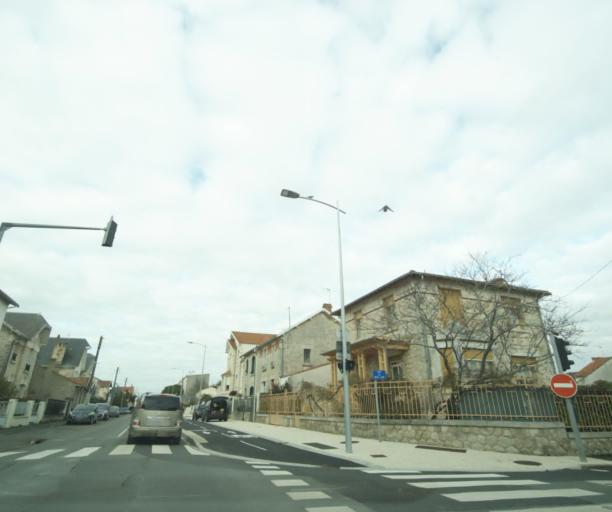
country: FR
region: Poitou-Charentes
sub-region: Departement de la Charente-Maritime
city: La Rochelle
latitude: 46.1673
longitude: -1.1638
